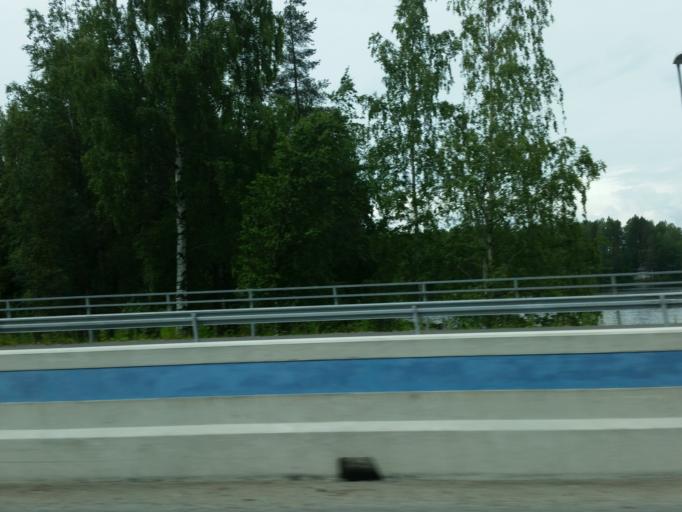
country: FI
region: Northern Savo
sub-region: Kuopio
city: Kuopio
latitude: 62.9667
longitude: 27.7005
